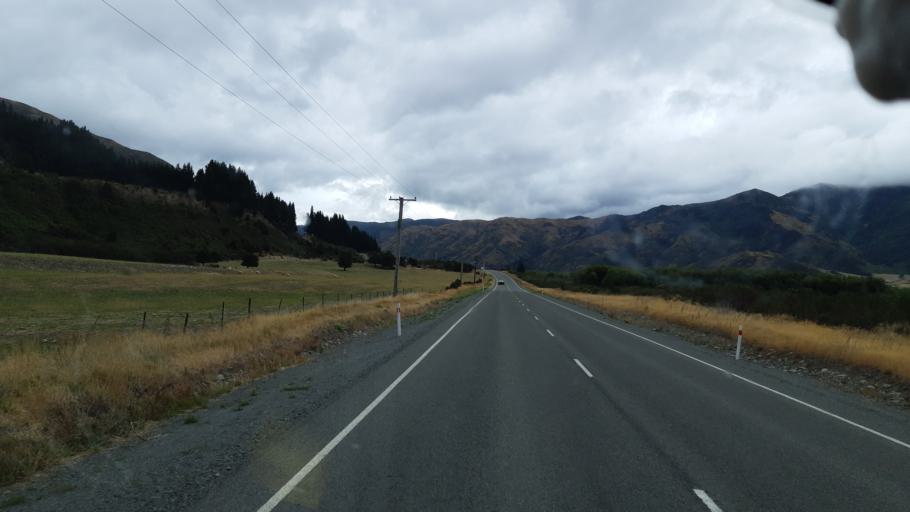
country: NZ
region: Canterbury
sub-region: Hurunui District
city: Amberley
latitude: -42.5709
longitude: 172.7047
